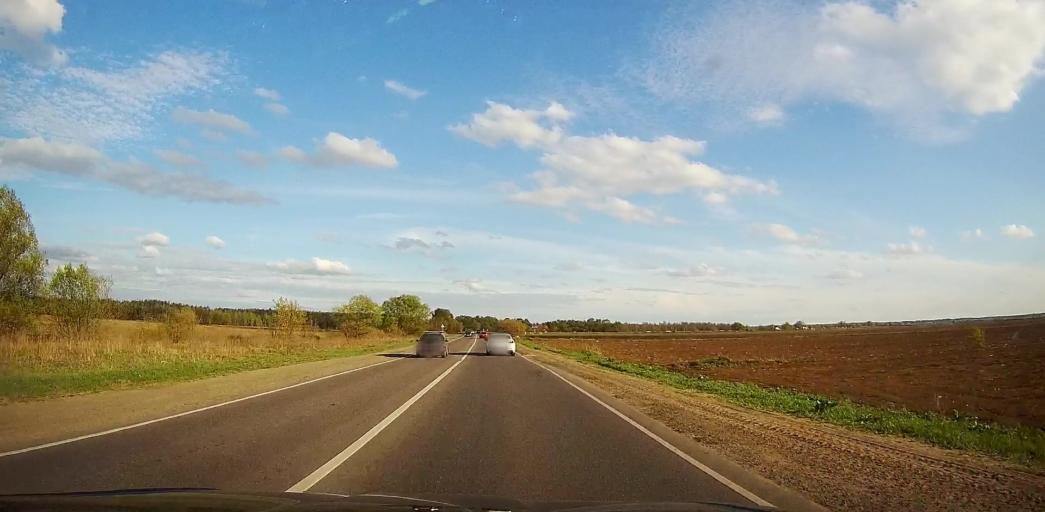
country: RU
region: Moskovskaya
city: Ramenskoye
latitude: 55.5342
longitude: 38.2781
